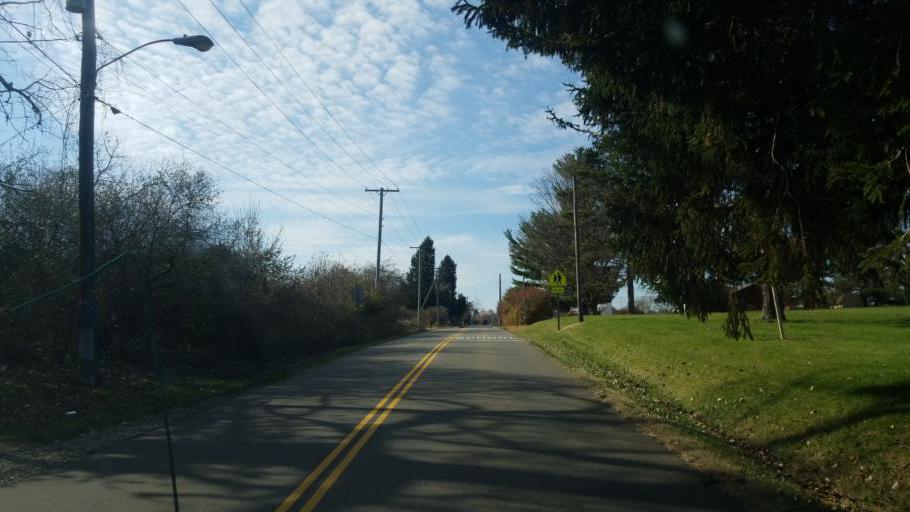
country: US
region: Ohio
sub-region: Richland County
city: Mansfield
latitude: 40.7211
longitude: -82.5232
